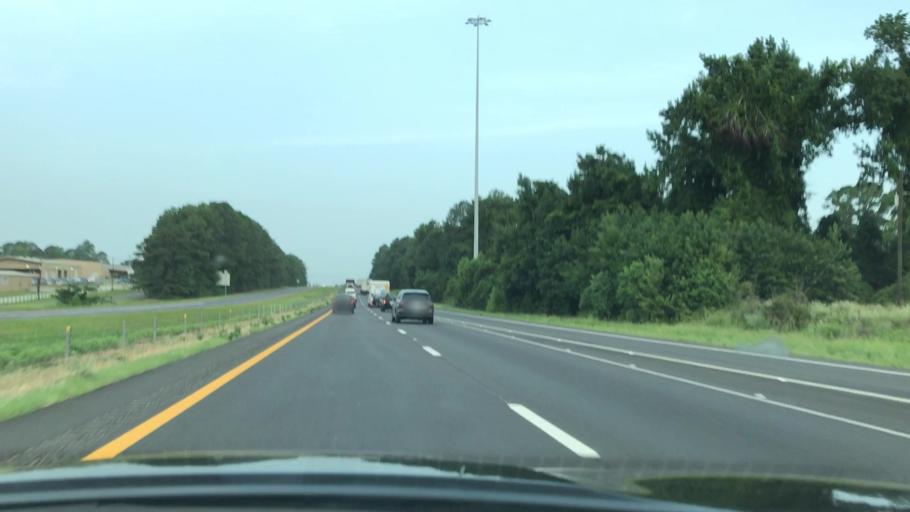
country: US
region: Texas
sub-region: Gregg County
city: Longview
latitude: 32.4597
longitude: -94.6707
